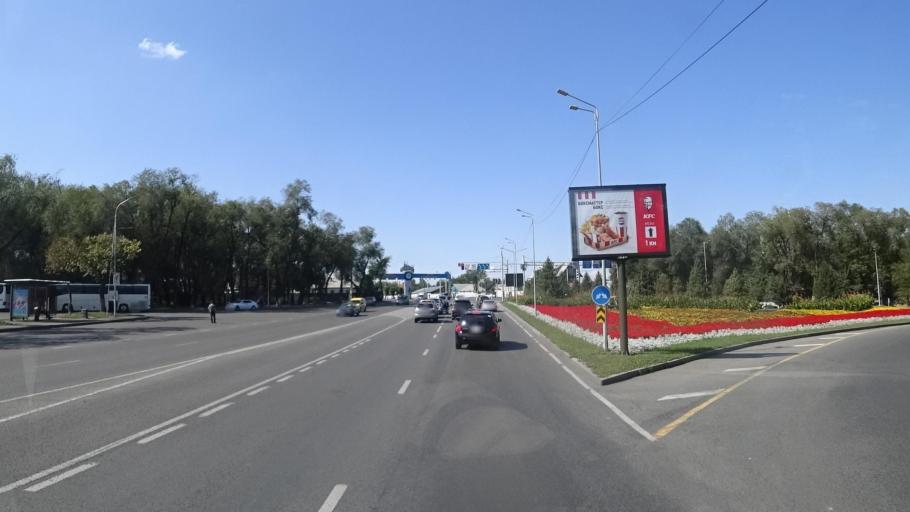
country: KZ
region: Almaty Oblysy
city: Pervomayskiy
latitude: 43.3426
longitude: 76.9959
